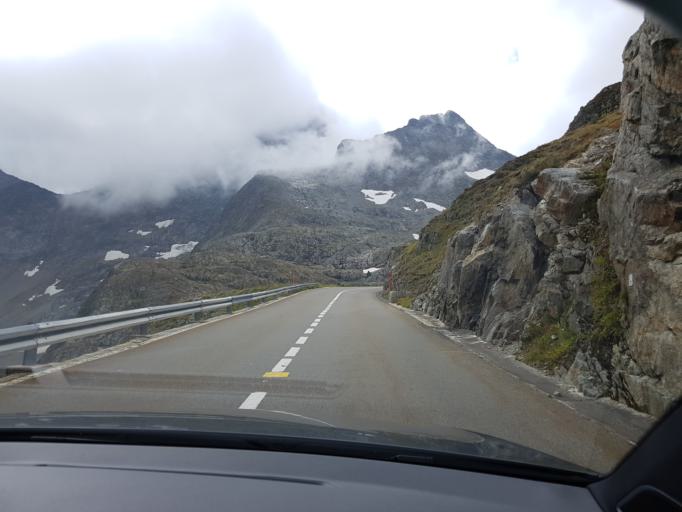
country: CH
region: Obwalden
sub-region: Obwalden
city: Engelberg
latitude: 46.7340
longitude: 8.4516
